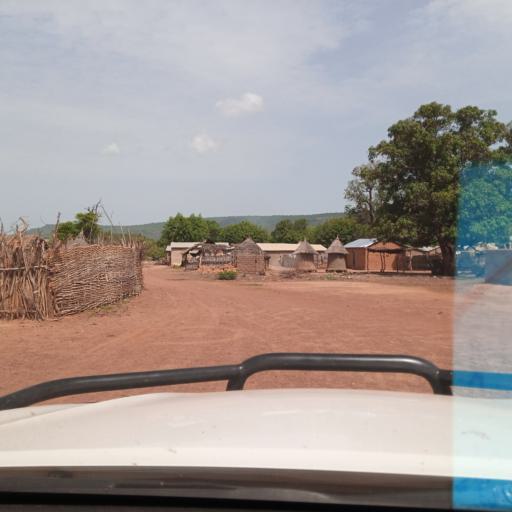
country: ML
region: Koulikoro
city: Kangaba
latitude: 12.3066
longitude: -8.9087
